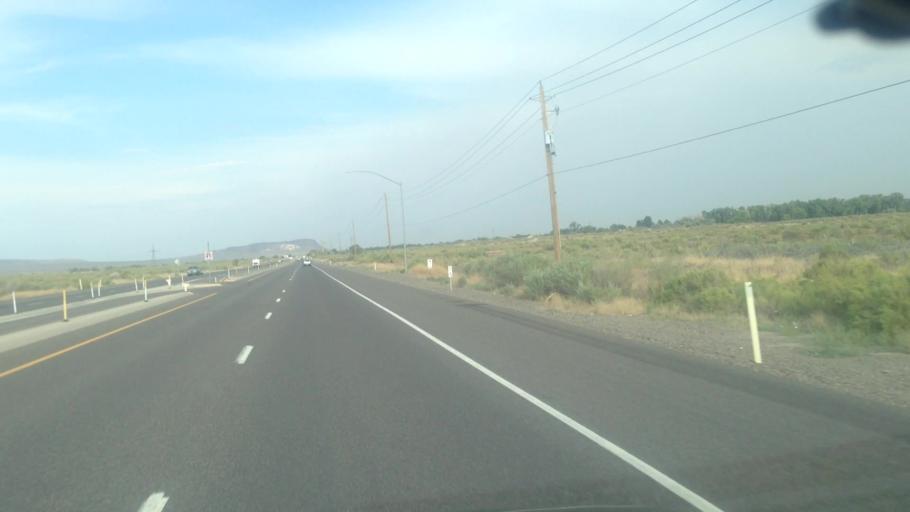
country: US
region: Nevada
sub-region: Lyon County
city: Fernley
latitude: 39.5961
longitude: -119.1812
